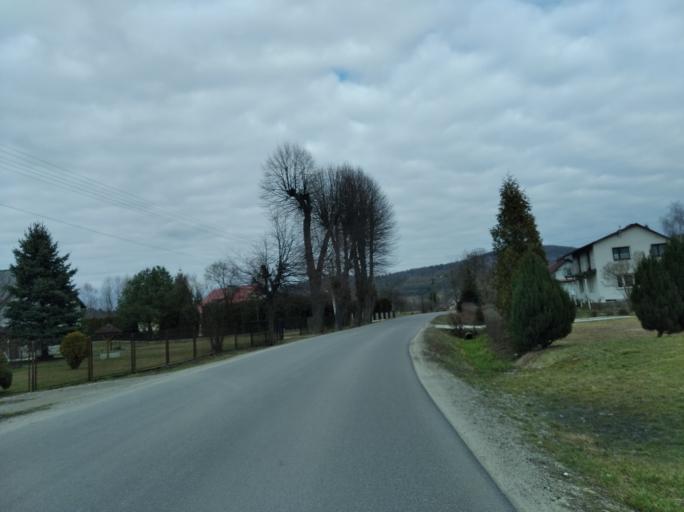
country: PL
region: Subcarpathian Voivodeship
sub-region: Powiat strzyzowski
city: Frysztak
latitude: 49.8394
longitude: 21.6210
